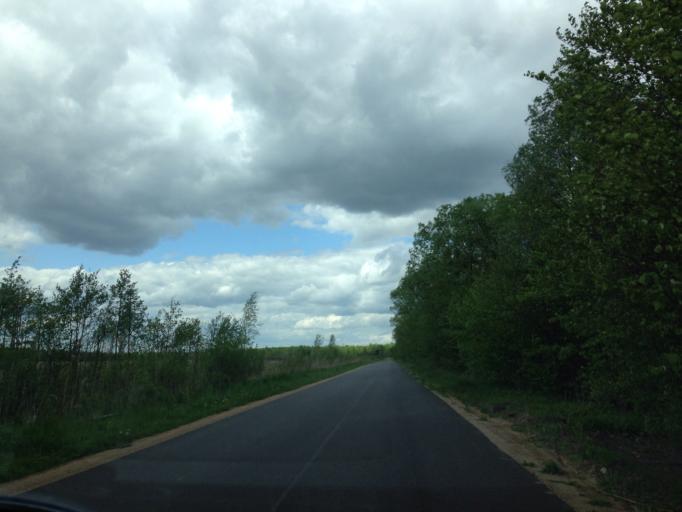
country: PL
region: Podlasie
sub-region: Powiat bialostocki
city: Tykocin
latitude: 53.2942
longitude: 22.6072
